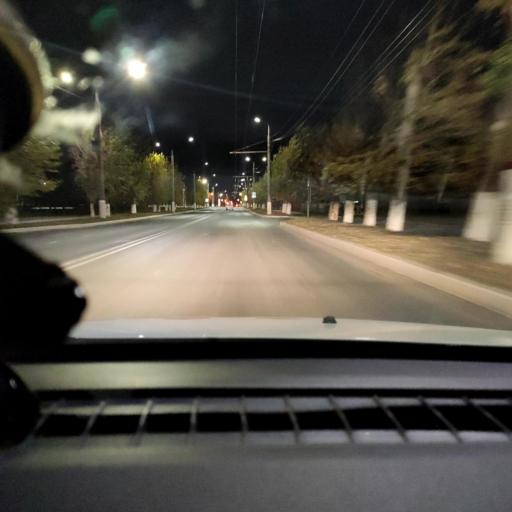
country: RU
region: Samara
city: Novokuybyshevsk
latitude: 53.1013
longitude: 49.9429
